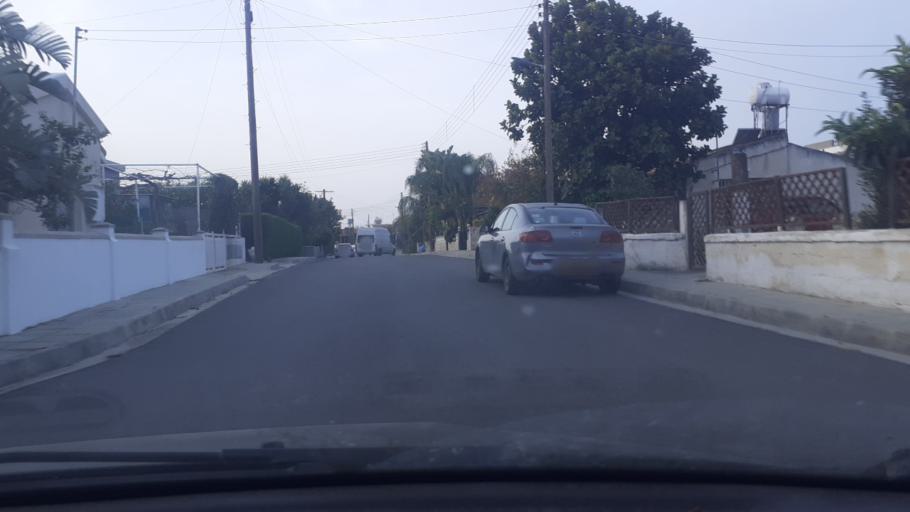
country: CY
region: Larnaka
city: Kolossi
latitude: 34.6620
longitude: 32.9585
